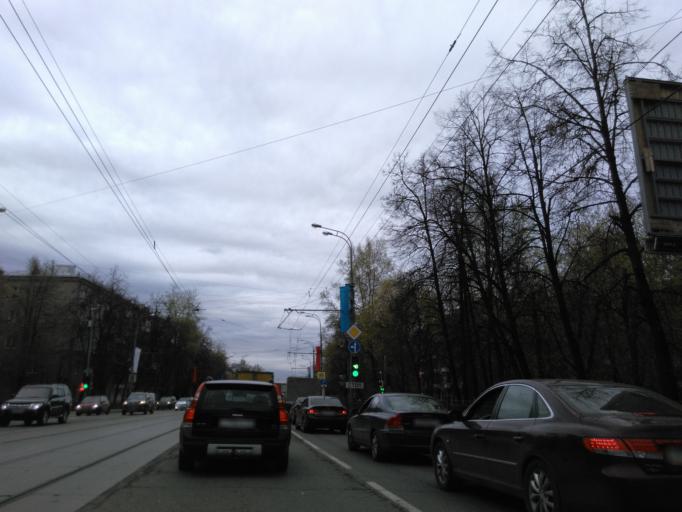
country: RU
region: Moscow
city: Pokrovskoye-Streshnevo
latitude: 55.8270
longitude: 37.4524
